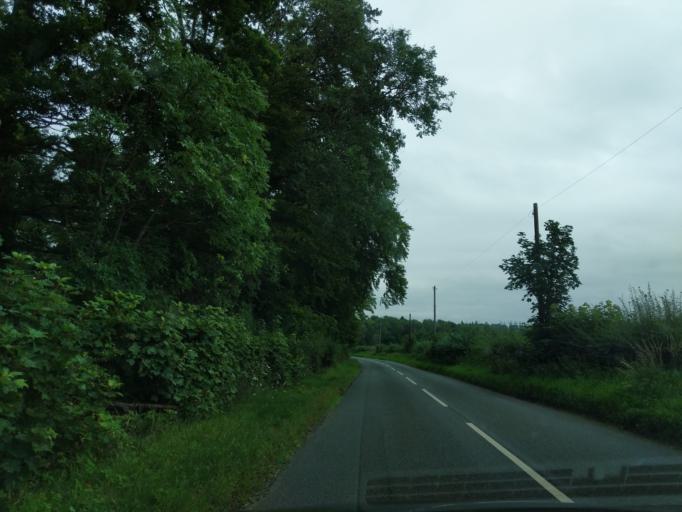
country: GB
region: Scotland
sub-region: East Lothian
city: Pencaitland
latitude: 55.8963
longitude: -2.8766
